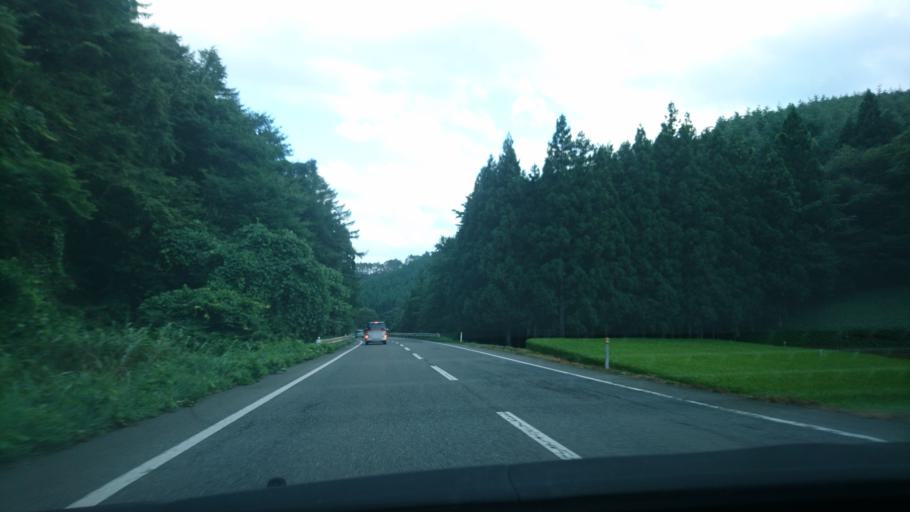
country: JP
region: Iwate
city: Mizusawa
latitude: 39.0531
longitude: 141.2274
